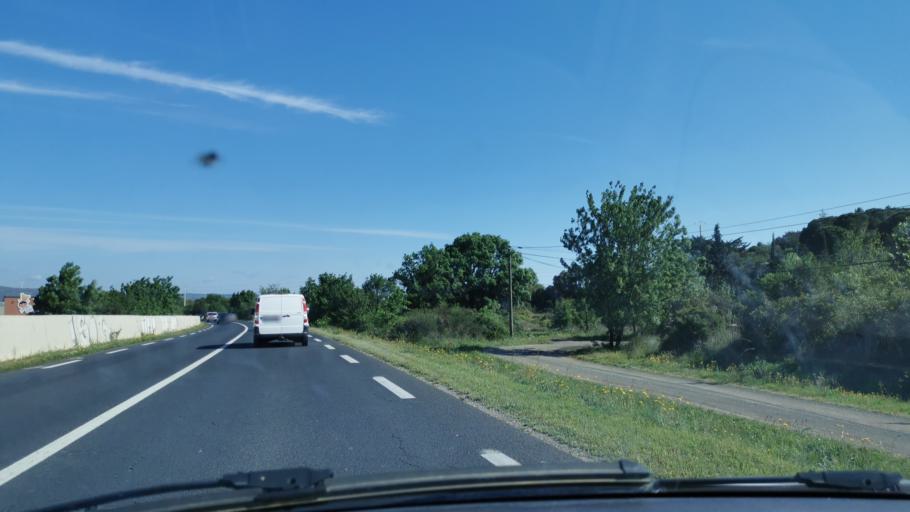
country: FR
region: Languedoc-Roussillon
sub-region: Departement de l'Herault
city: Balaruc-le-Vieux
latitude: 43.4648
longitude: 3.6926
